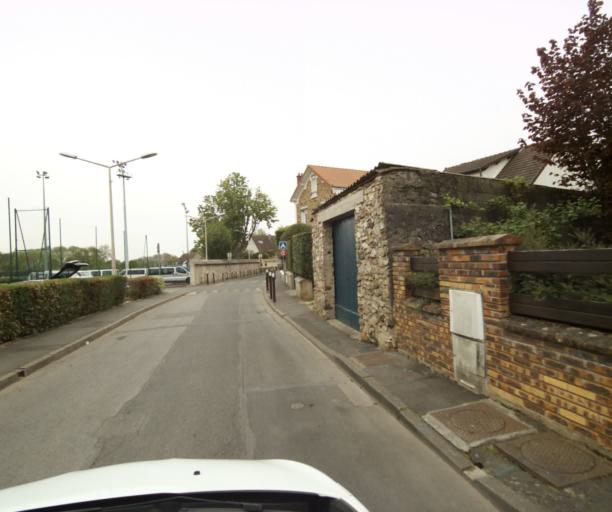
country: FR
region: Ile-de-France
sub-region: Departement de Seine-et-Marne
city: Torcy
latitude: 48.8533
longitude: 2.6517
